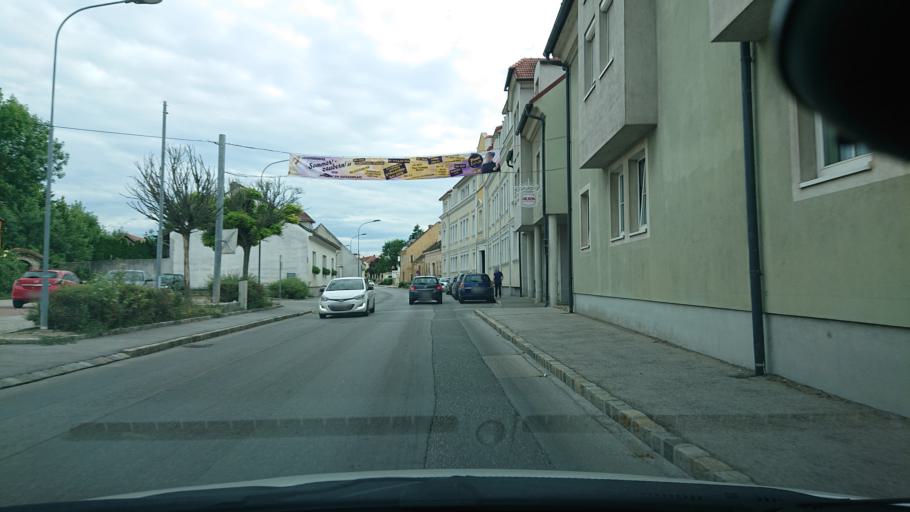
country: AT
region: Lower Austria
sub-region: Politischer Bezirk Baden
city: Leobersdorf
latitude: 47.9254
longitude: 16.2155
